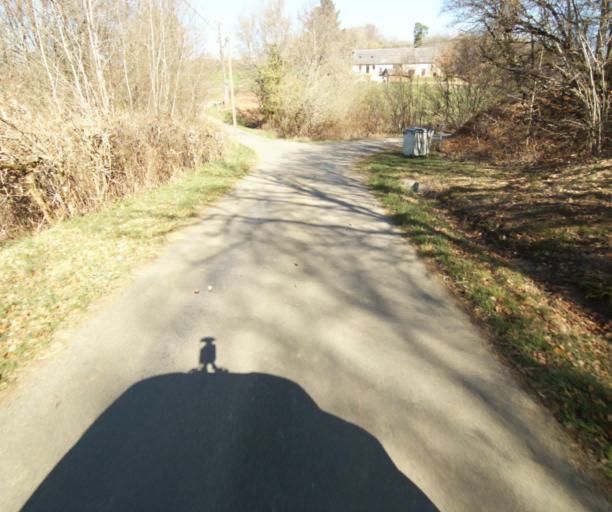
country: FR
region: Limousin
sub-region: Departement de la Correze
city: Chamboulive
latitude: 45.4050
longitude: 1.7338
